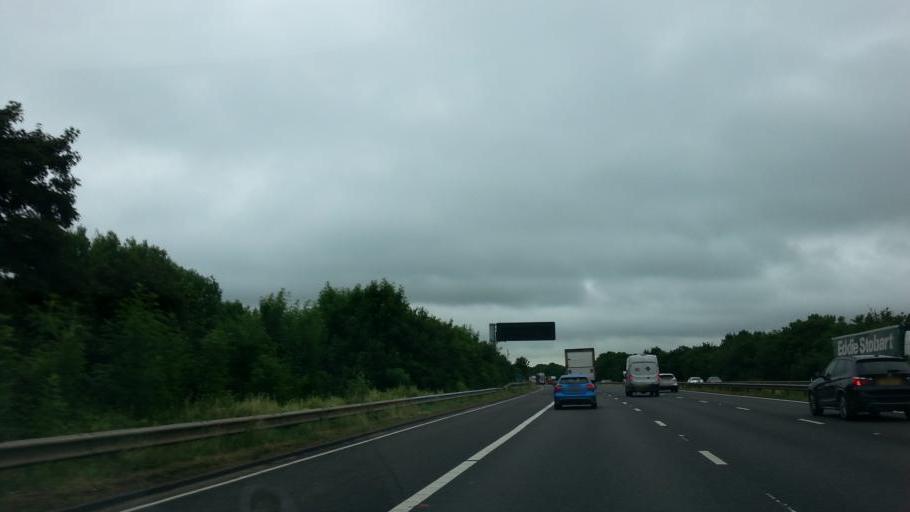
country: GB
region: England
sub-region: Leicestershire
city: Cosby
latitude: 52.5476
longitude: -1.1856
